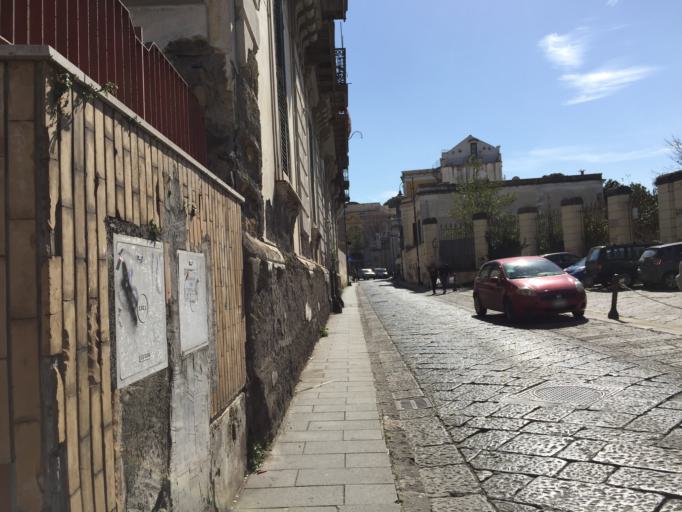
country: IT
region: Campania
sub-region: Provincia di Napoli
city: San Giorgio a Cremano
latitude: 40.8292
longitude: 14.3391
